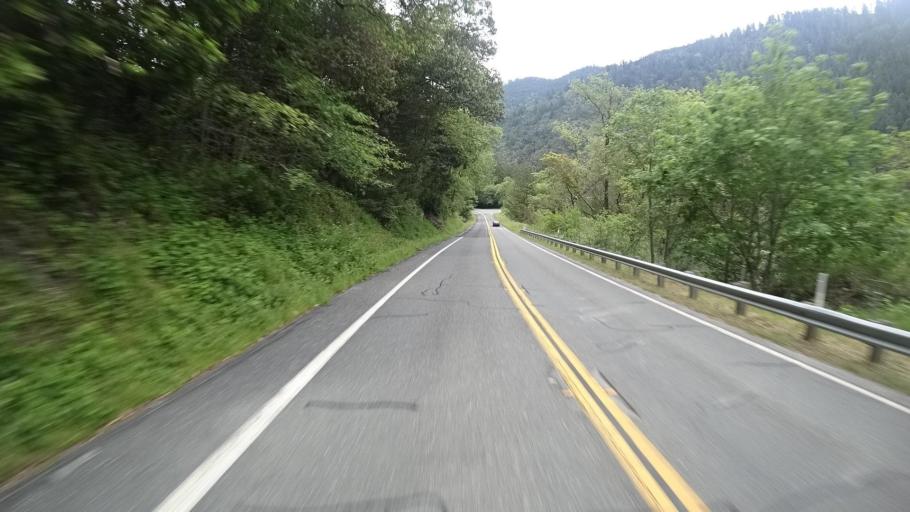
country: US
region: California
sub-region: Humboldt County
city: Willow Creek
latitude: 41.1892
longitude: -123.6846
